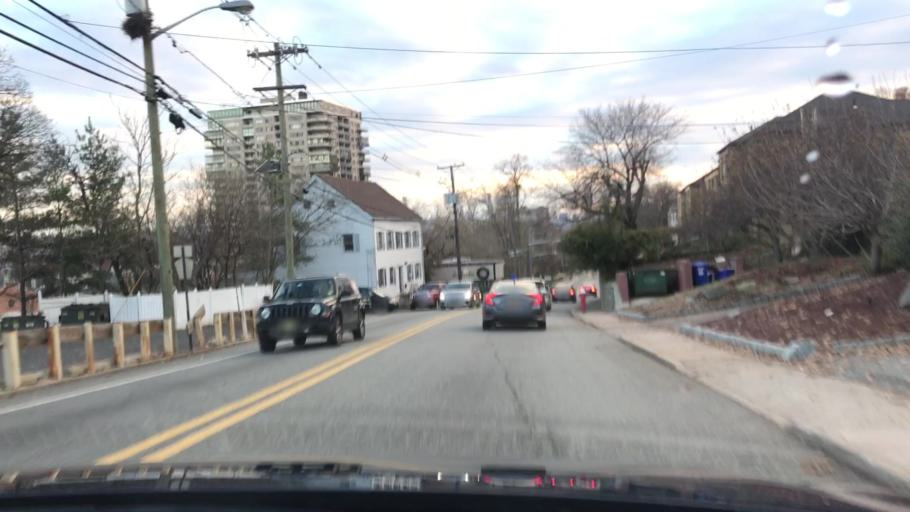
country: US
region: New Jersey
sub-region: Bergen County
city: Edgewater
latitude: 40.8380
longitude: -73.9703
